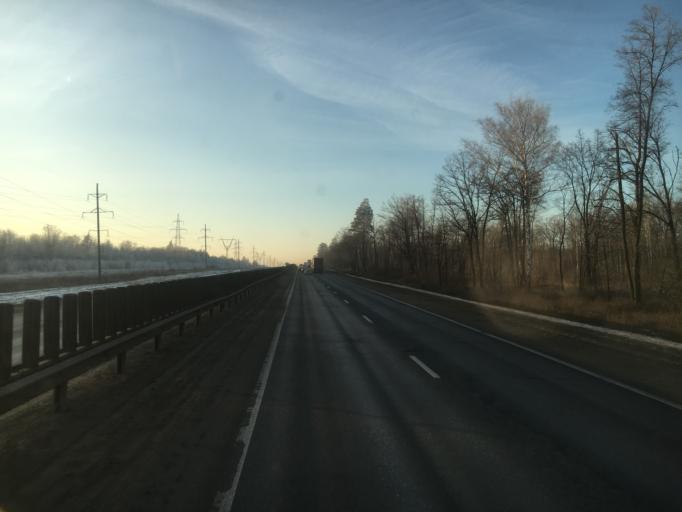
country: RU
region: Samara
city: Pribrezhnyy
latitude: 53.5154
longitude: 49.8748
